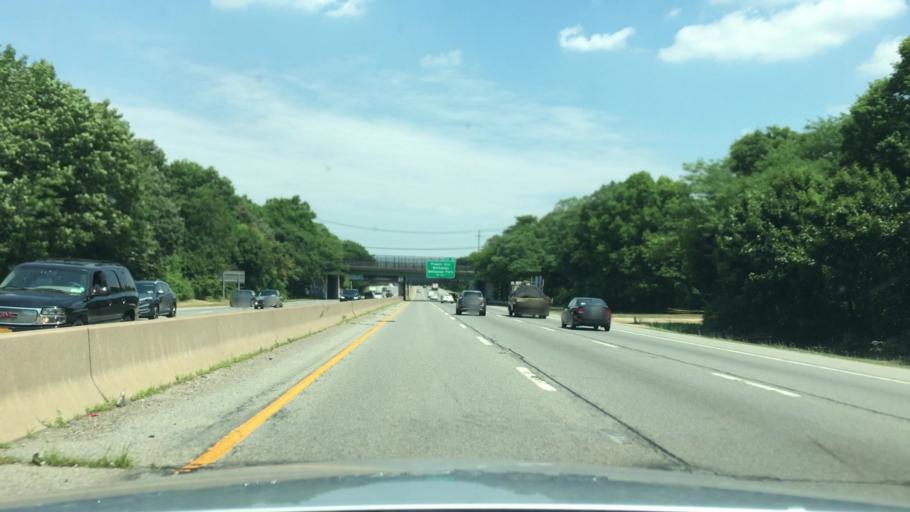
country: US
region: New York
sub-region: Nassau County
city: Bethpage
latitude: 40.7347
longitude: -73.4742
